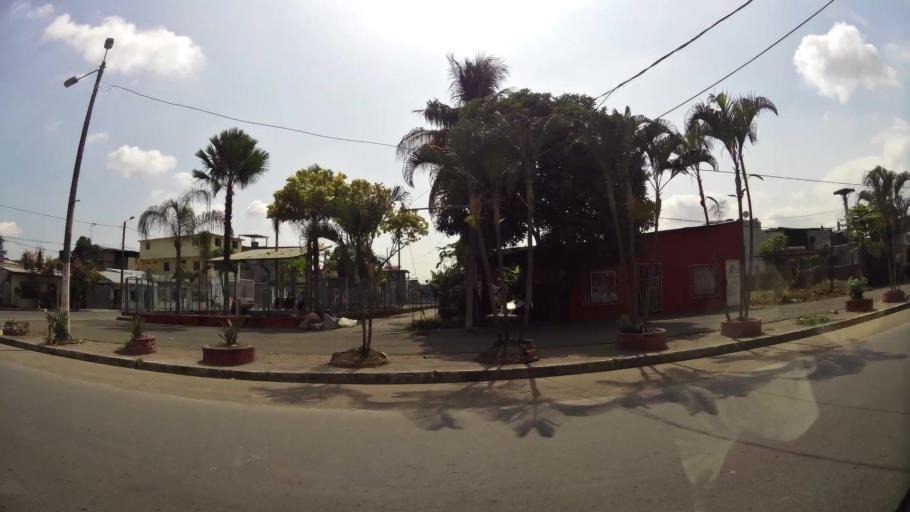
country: EC
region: Guayas
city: Eloy Alfaro
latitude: -2.1596
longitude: -79.8329
